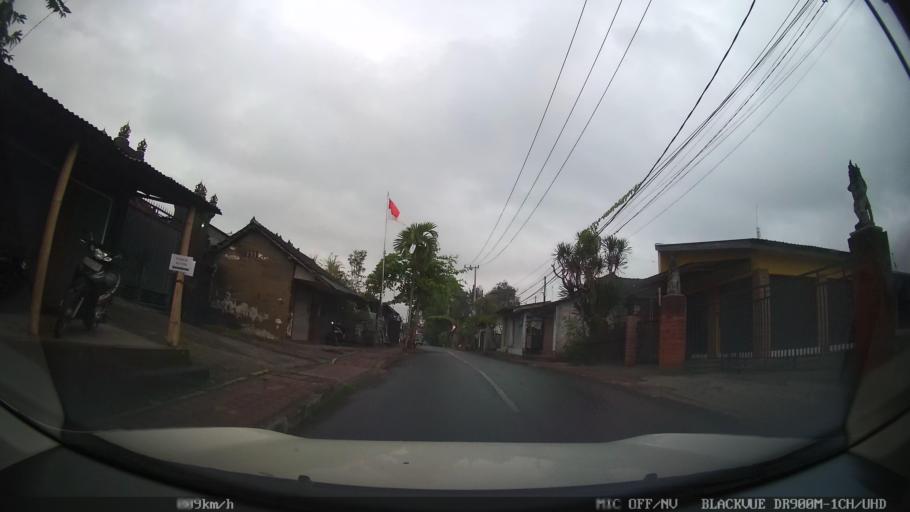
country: ID
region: Bali
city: Banjar Desa
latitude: -8.5894
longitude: 115.2797
